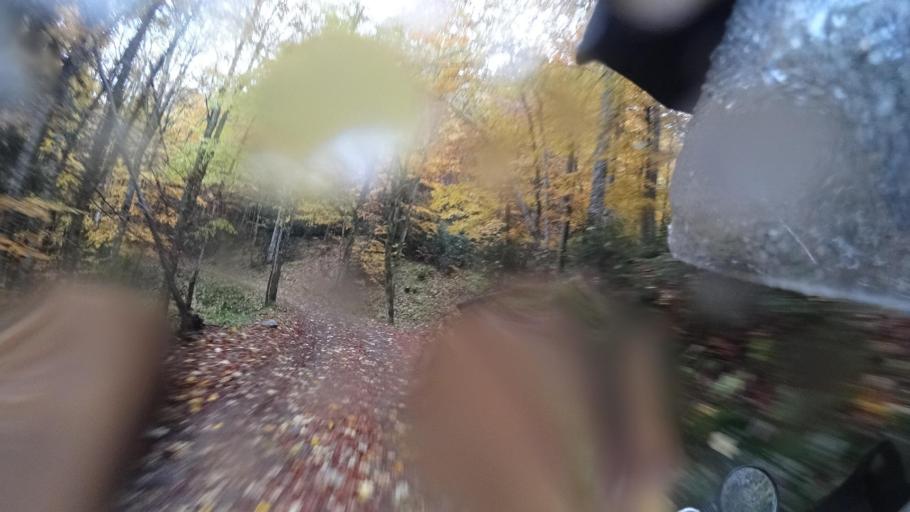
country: HR
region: Primorsko-Goranska
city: Vrbovsko
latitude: 45.3045
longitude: 15.0633
